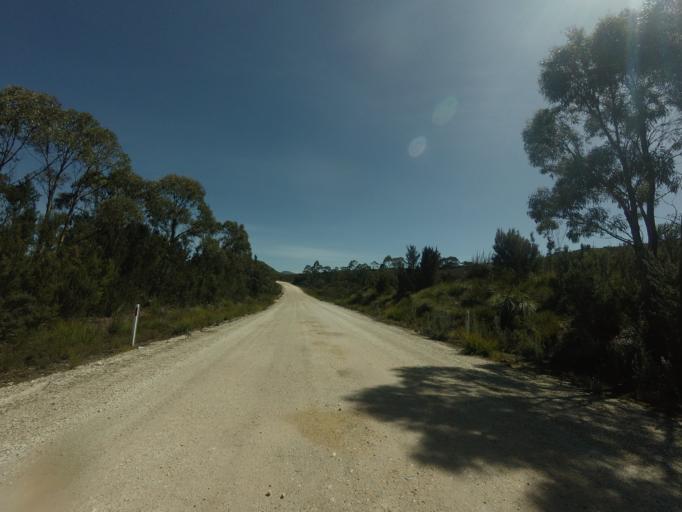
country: AU
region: Tasmania
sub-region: Huon Valley
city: Geeveston
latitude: -43.0335
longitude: 146.3087
